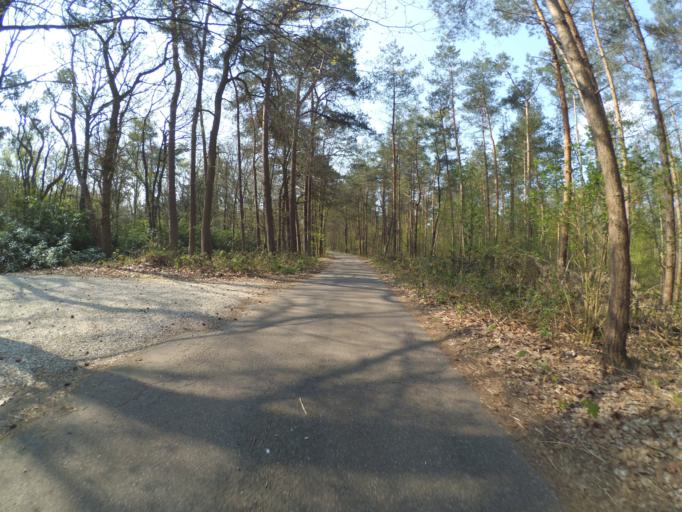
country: NL
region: Utrecht
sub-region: Gemeente Amersfoort
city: Amersfoort
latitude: 52.1360
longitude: 5.3546
